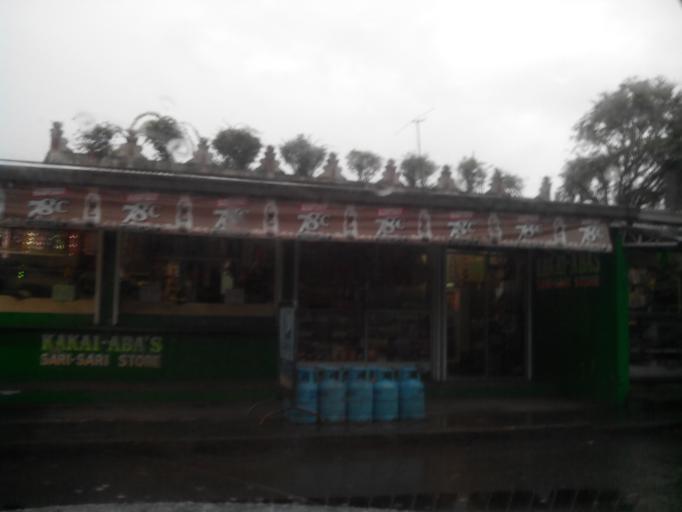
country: PH
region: Calabarzon
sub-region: Province of Rizal
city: Taytay
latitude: 14.5650
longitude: 121.1342
